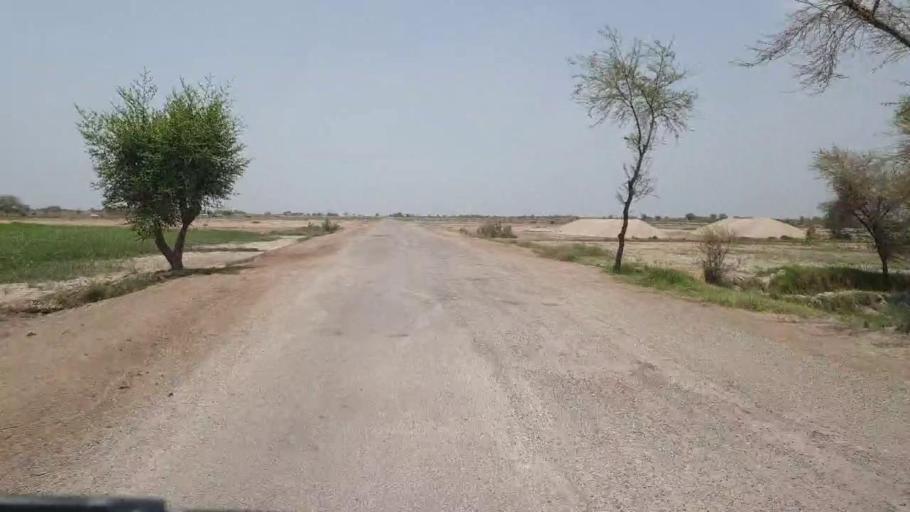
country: PK
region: Sindh
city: Daulatpur
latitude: 26.4474
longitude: 68.1164
